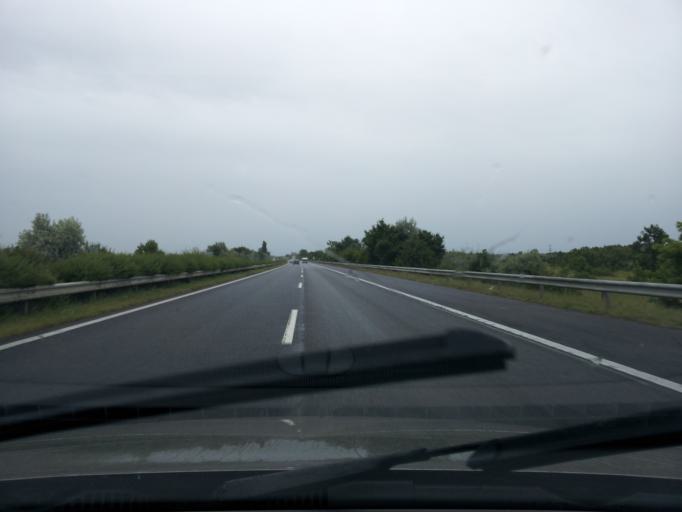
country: HU
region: Fejer
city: Lepseny
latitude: 47.0025
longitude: 18.2174
